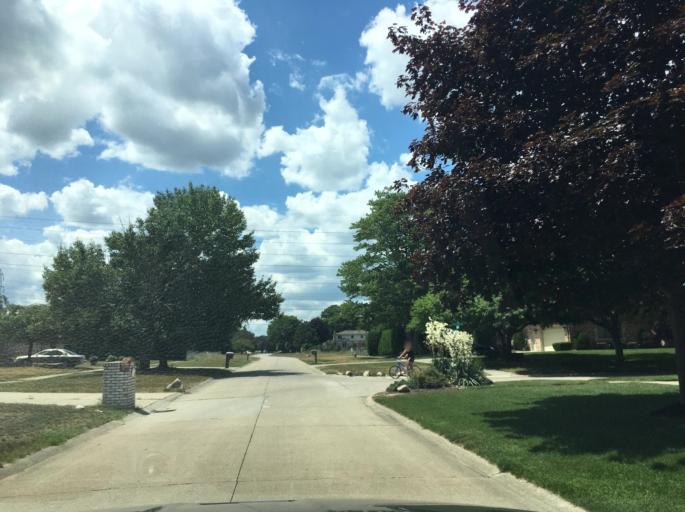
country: US
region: Michigan
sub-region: Macomb County
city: Utica
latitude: 42.6343
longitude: -83.0008
